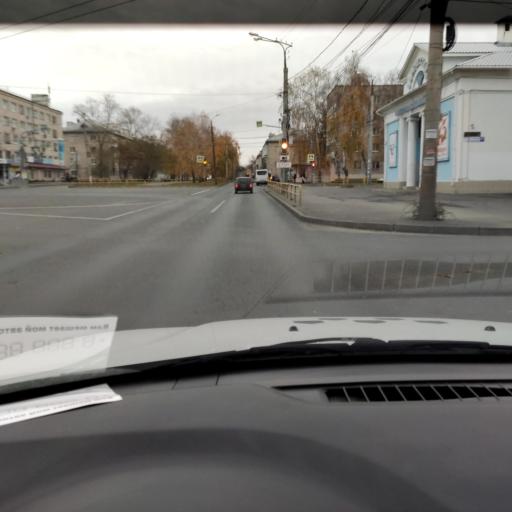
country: RU
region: Samara
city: Tol'yatti
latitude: 53.5186
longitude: 49.4038
